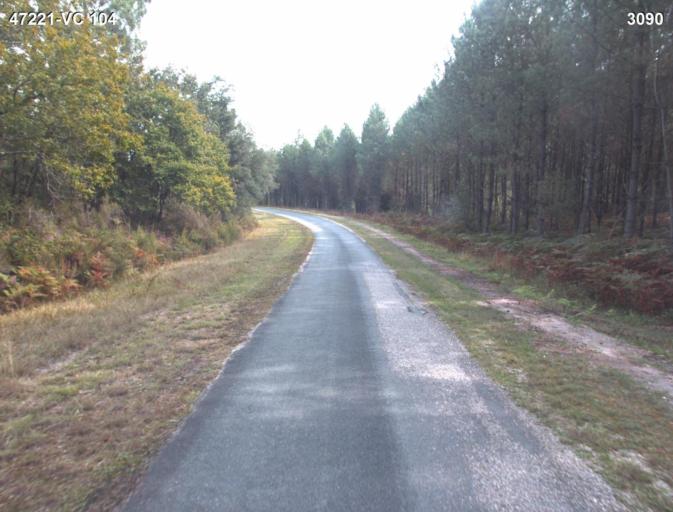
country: FR
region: Aquitaine
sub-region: Departement du Lot-et-Garonne
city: Mezin
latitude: 44.1235
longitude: 0.1906
